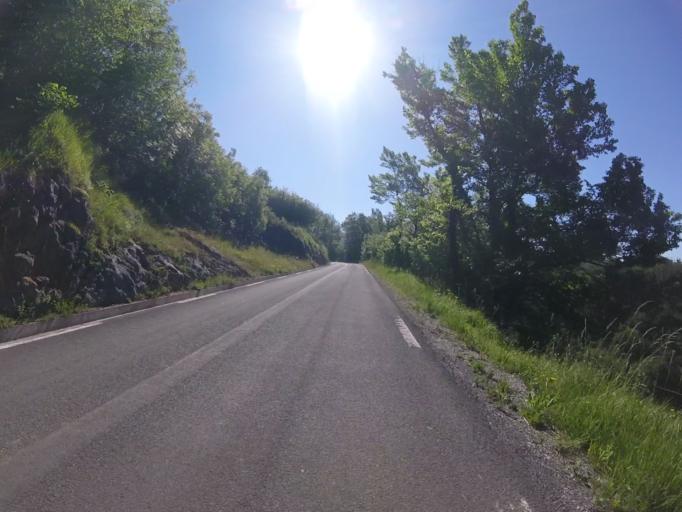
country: ES
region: Basque Country
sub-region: Provincia de Guipuzcoa
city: Beizama
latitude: 43.1240
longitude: -2.1908
